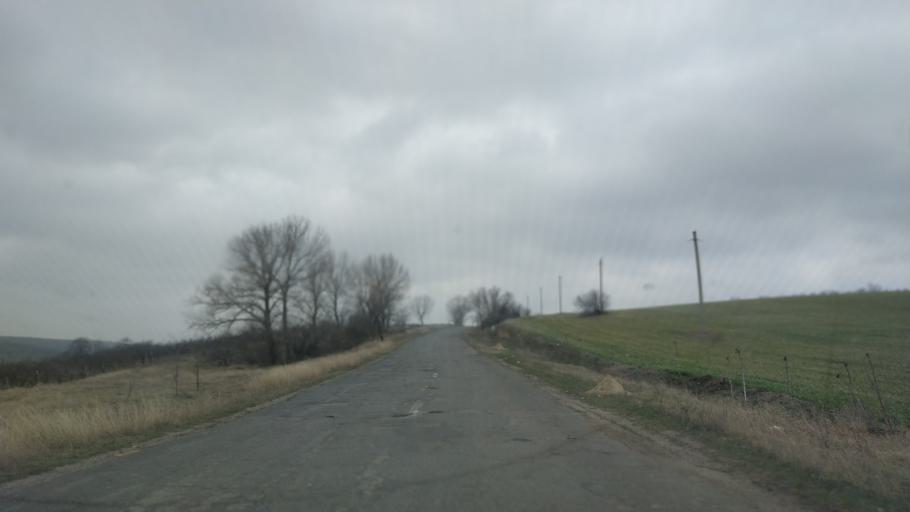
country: MD
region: Gagauzia
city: Bugeac
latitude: 46.3546
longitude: 28.7939
